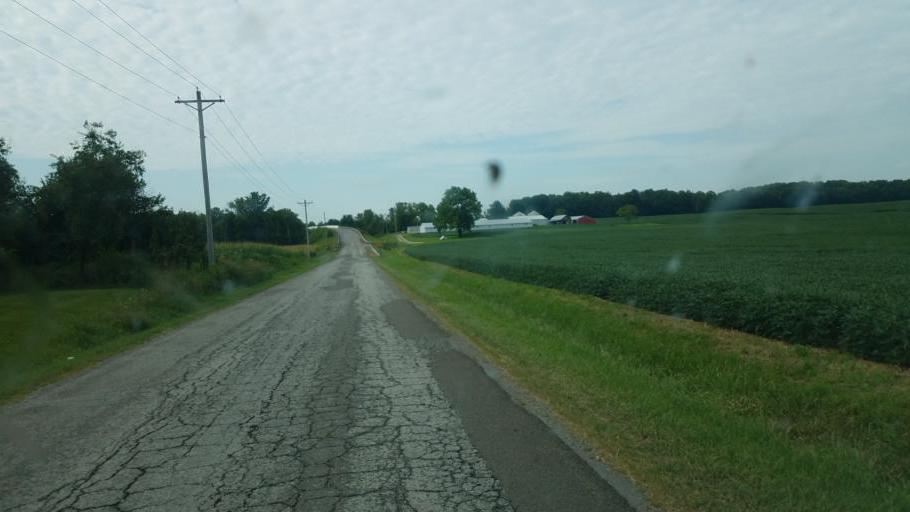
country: US
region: Ohio
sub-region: Morrow County
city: Mount Gilead
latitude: 40.4728
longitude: -82.7579
